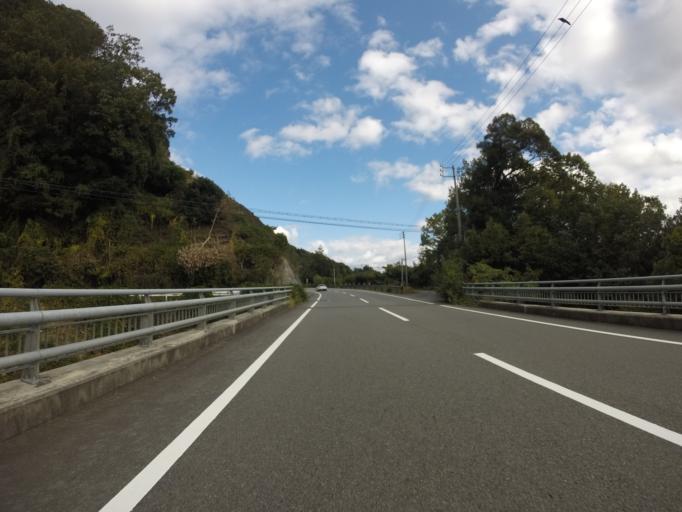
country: JP
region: Shizuoka
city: Kanaya
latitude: 34.8810
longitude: 138.1001
